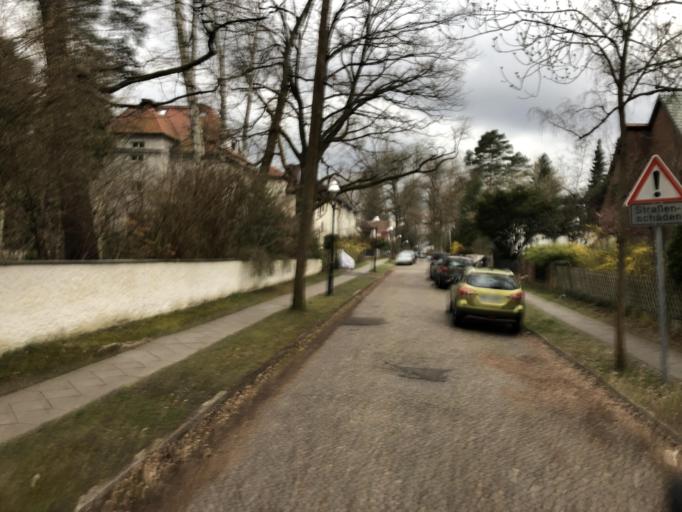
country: DE
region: Berlin
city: Frohnau
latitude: 52.6404
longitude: 13.2957
